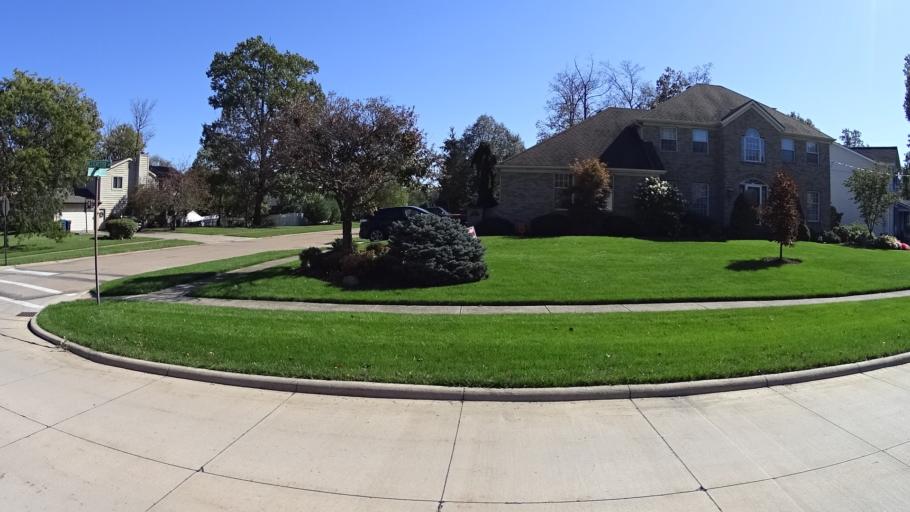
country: US
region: Ohio
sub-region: Lorain County
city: Amherst
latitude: 41.3859
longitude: -82.2286
